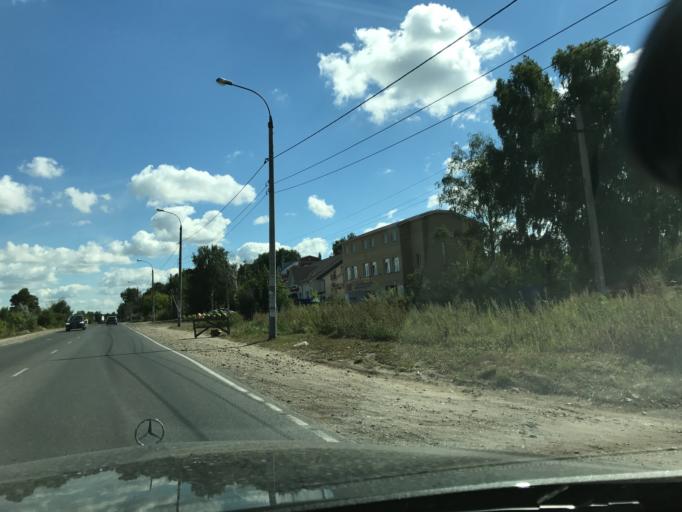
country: RU
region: Nizjnij Novgorod
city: Gorbatovka
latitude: 56.2130
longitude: 43.7625
